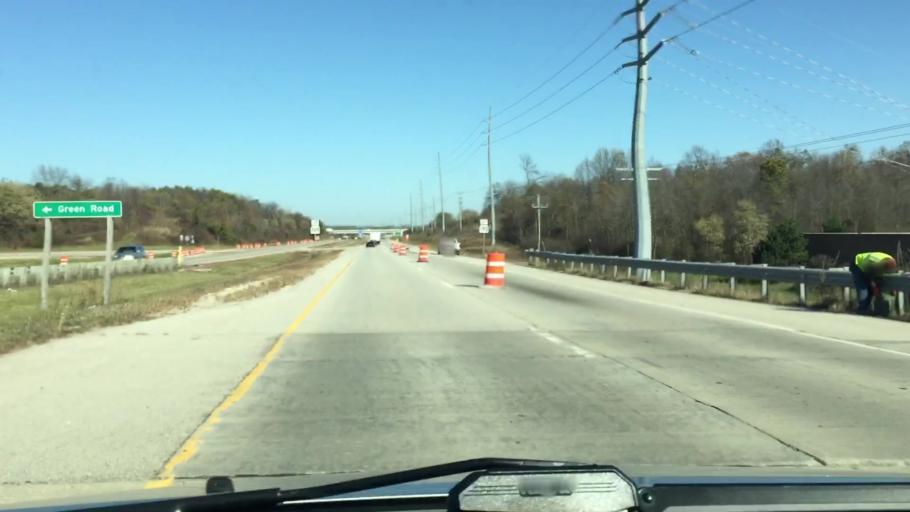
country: US
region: Wisconsin
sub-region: Waukesha County
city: Pewaukee
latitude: 43.0760
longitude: -88.2056
